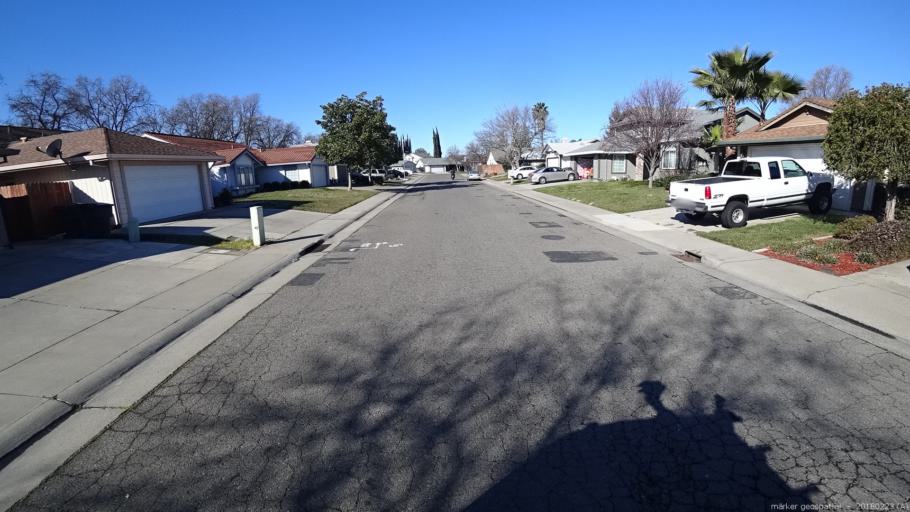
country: US
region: California
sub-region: Sacramento County
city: North Highlands
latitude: 38.7044
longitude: -121.3674
